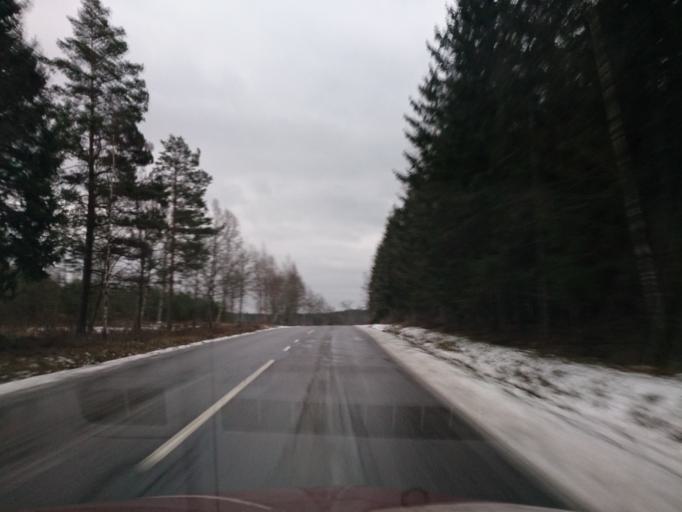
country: SE
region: OEstergoetland
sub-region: Atvidabergs Kommun
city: Atvidaberg
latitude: 58.3605
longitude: 16.0291
